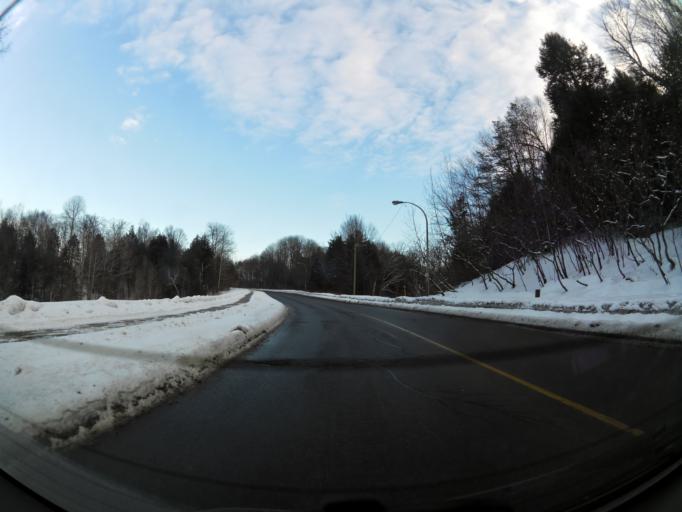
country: CA
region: Quebec
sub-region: Outaouais
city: Gatineau
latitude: 45.4587
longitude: -75.5480
